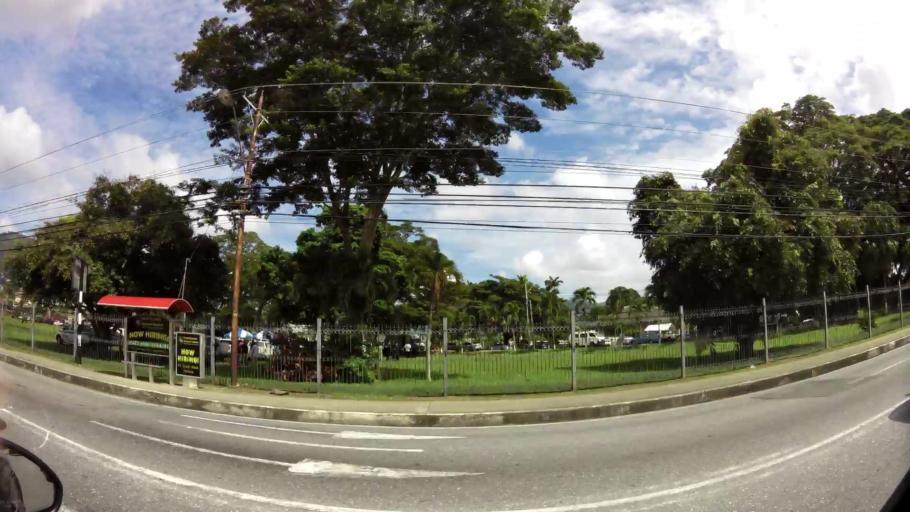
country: TT
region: City of Port of Spain
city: Port-of-Spain
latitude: 10.6697
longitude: -61.5284
